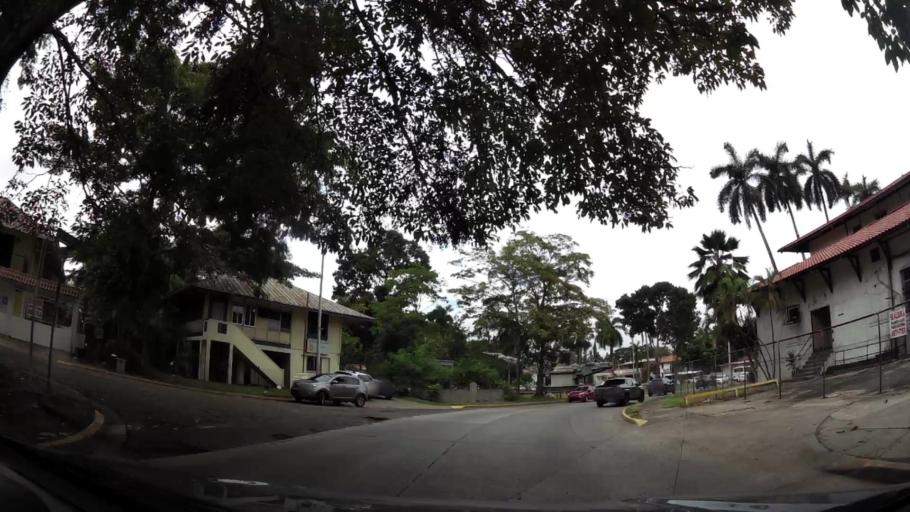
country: PA
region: Panama
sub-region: Distrito de Panama
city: Ancon
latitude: 8.9512
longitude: -79.5564
